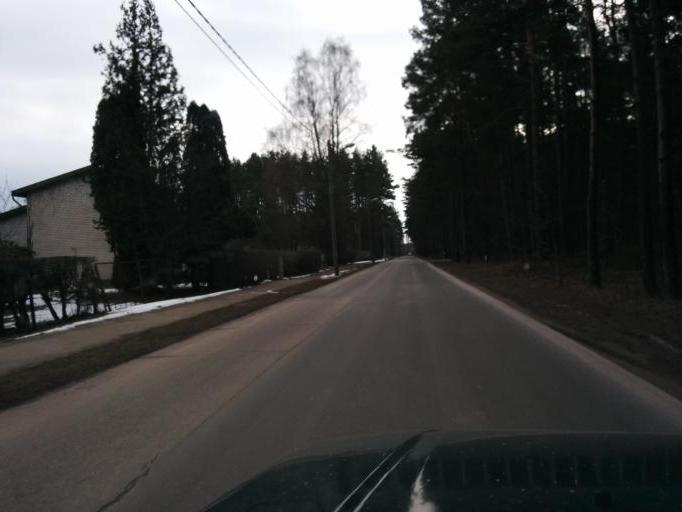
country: LV
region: Jurmala
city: Jurmala
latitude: 56.9498
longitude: 23.7254
